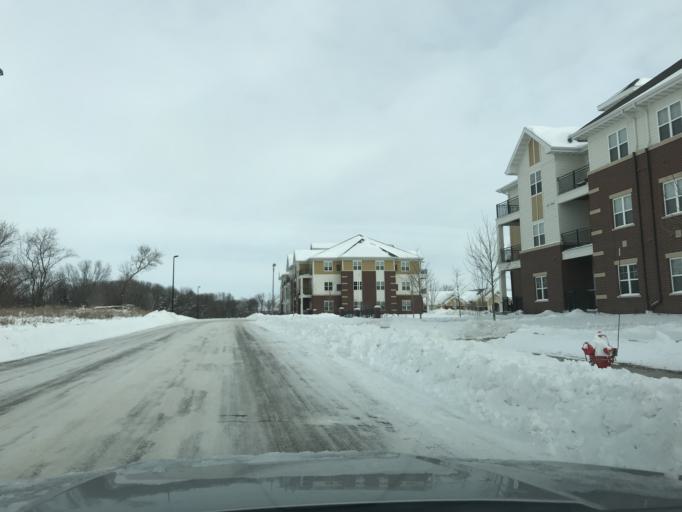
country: US
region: Wisconsin
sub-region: Dane County
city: Sun Prairie
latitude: 43.1643
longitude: -89.2617
